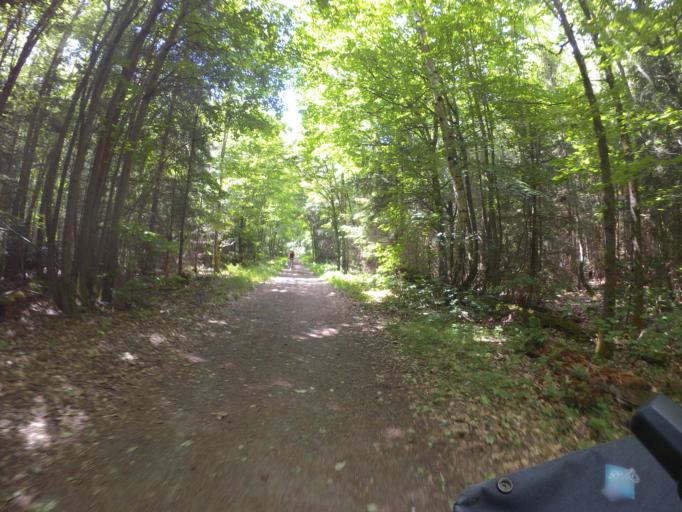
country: DE
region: Rheinland-Pfalz
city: Rodenbach
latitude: 49.4647
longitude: 7.6766
